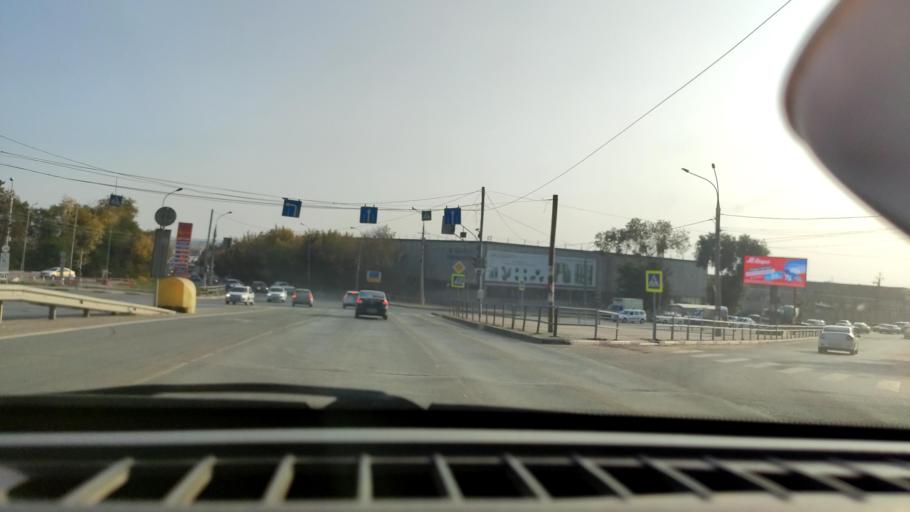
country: RU
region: Samara
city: Samara
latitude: 53.1801
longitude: 50.1918
